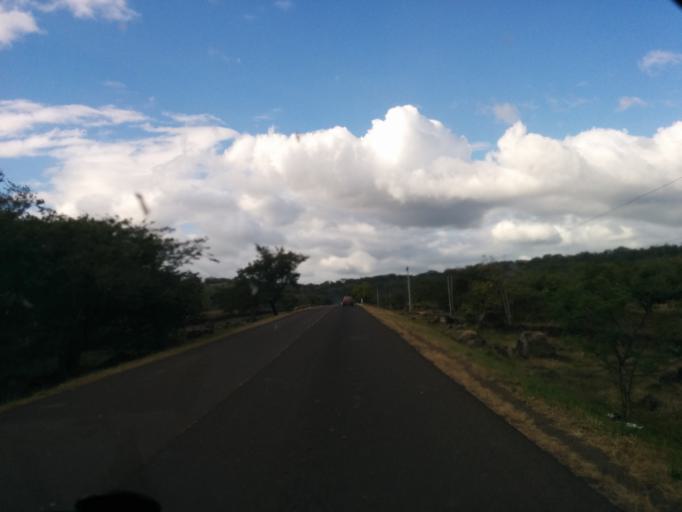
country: NI
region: Esteli
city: Esteli
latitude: 13.1993
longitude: -86.3745
